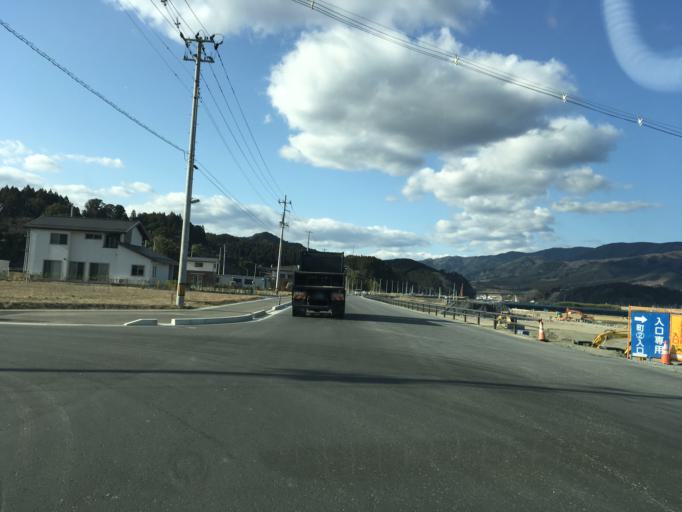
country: JP
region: Iwate
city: Ofunato
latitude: 39.0056
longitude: 141.6173
